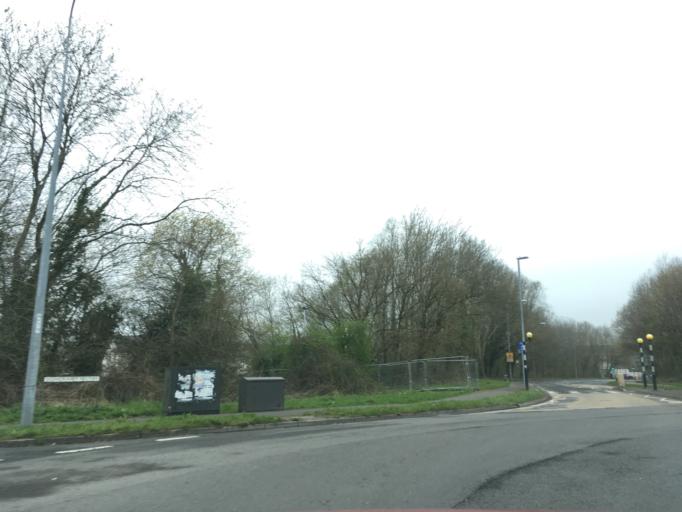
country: GB
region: Wales
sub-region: Newport
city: Newport
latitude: 51.5555
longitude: -3.0241
